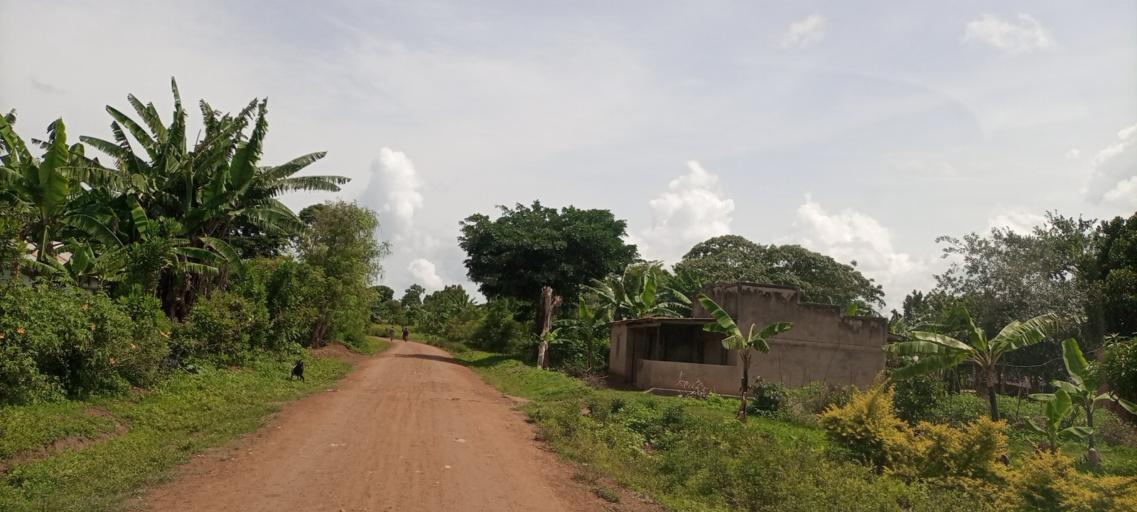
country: UG
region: Eastern Region
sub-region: Budaka District
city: Budaka
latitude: 1.1696
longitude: 33.9408
